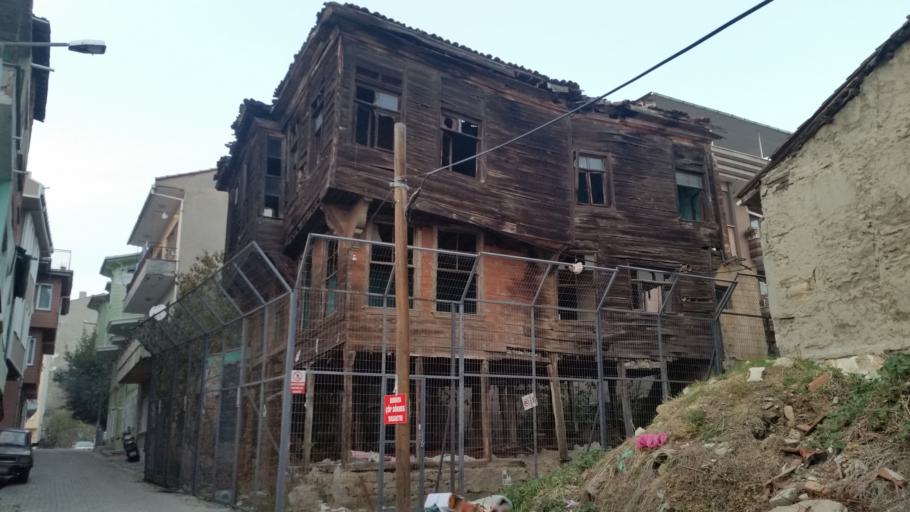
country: TR
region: Tekirdag
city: Tekirdag
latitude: 40.9743
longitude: 27.5094
